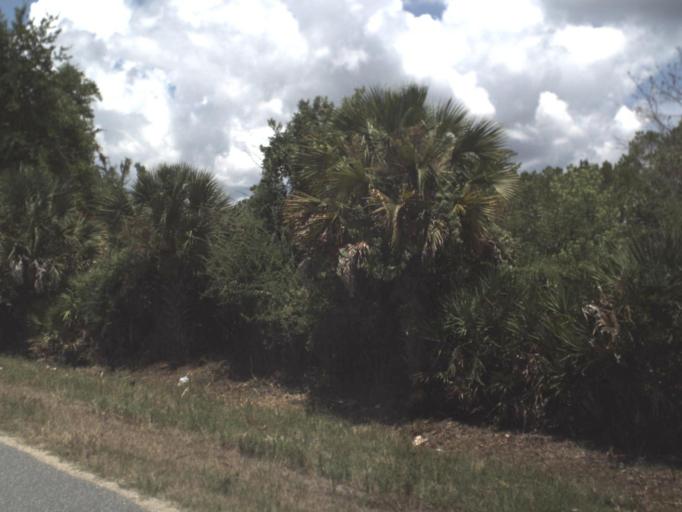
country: US
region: Florida
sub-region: Leon County
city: Woodville
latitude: 30.1443
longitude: -83.9458
